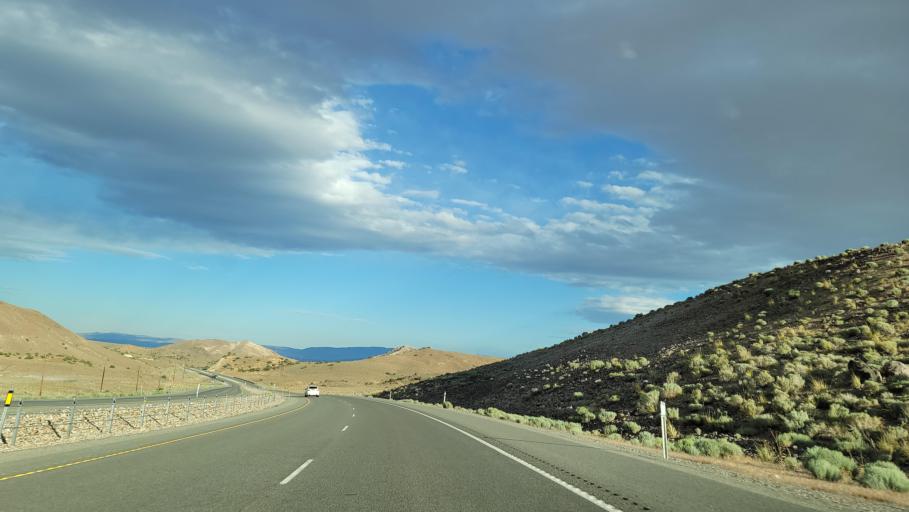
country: US
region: Nevada
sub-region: Lyon County
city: Stagecoach
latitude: 39.4741
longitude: -119.3979
